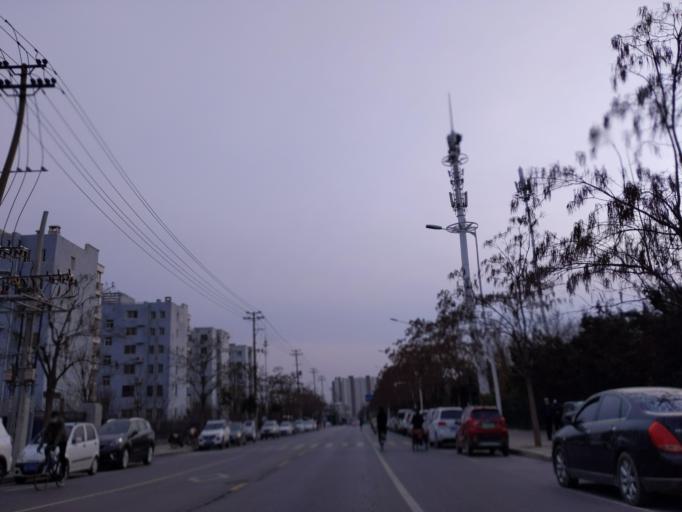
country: CN
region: Henan Sheng
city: Zhongyuanlu
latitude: 35.7590
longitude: 115.0407
